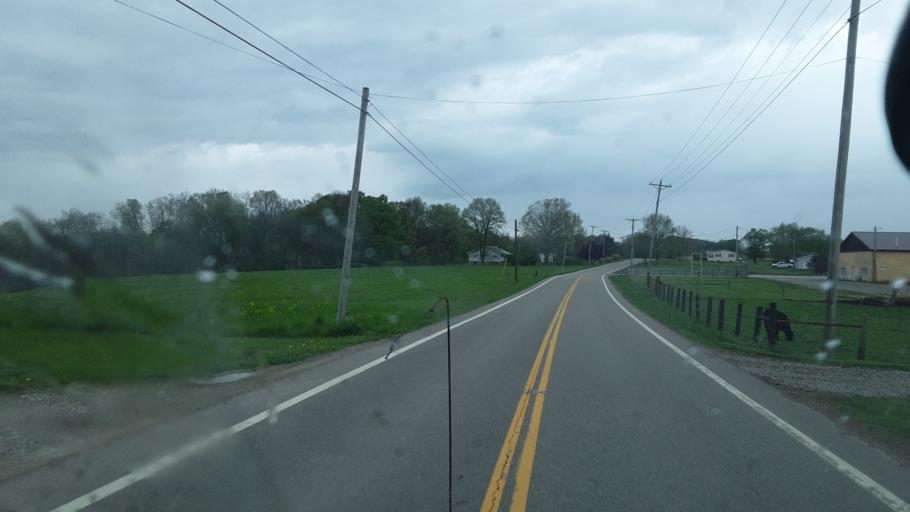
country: US
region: Ohio
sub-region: Muskingum County
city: New Concord
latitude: 39.9282
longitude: -81.6795
